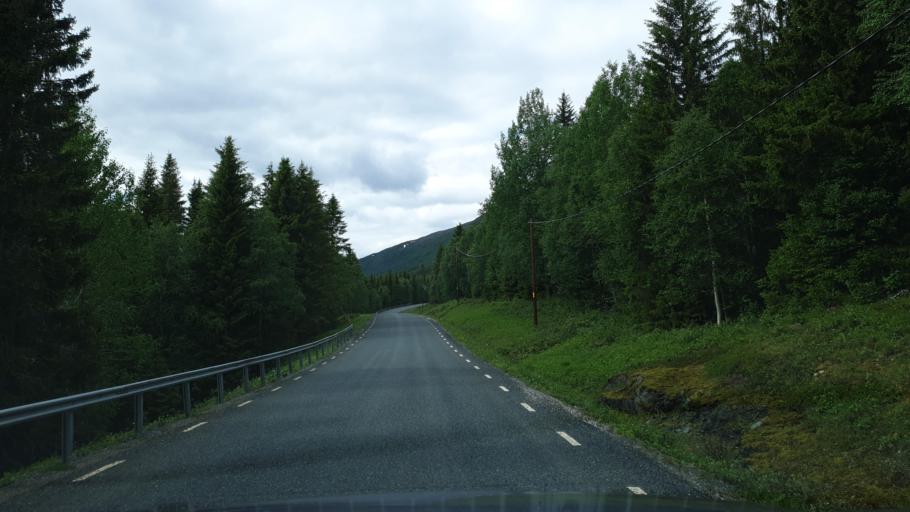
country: NO
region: Nordland
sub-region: Hattfjelldal
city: Hattfjelldal
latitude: 65.4357
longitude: 14.5750
